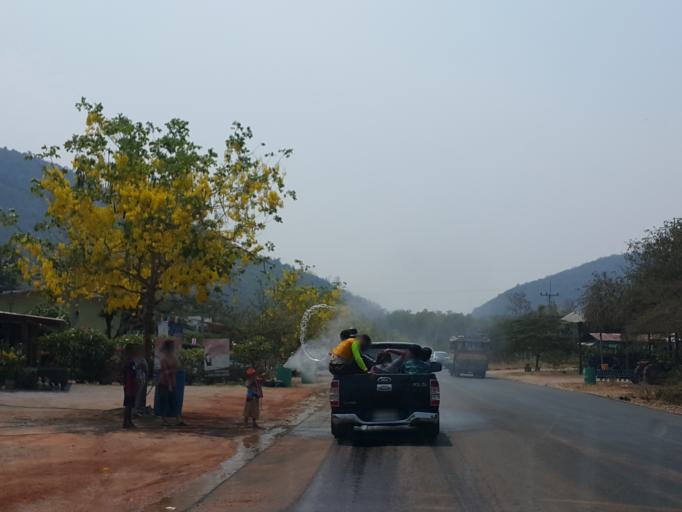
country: TH
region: Nakhon Sawan
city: Mae Wong
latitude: 15.8996
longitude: 99.4661
